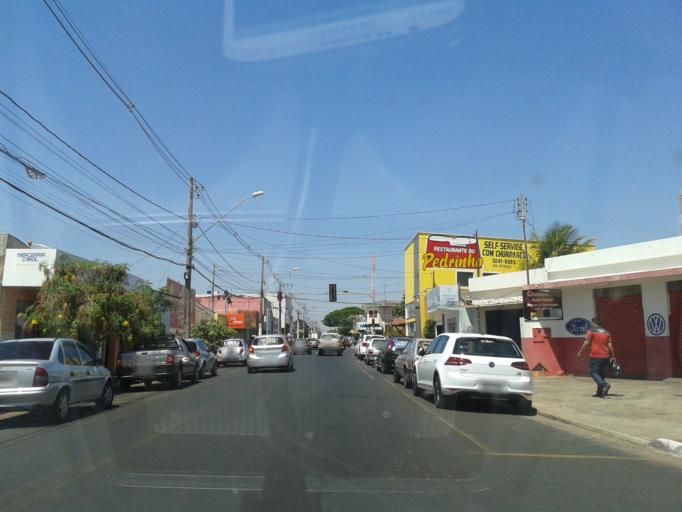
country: BR
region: Minas Gerais
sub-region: Araguari
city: Araguari
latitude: -18.6645
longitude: -48.1833
